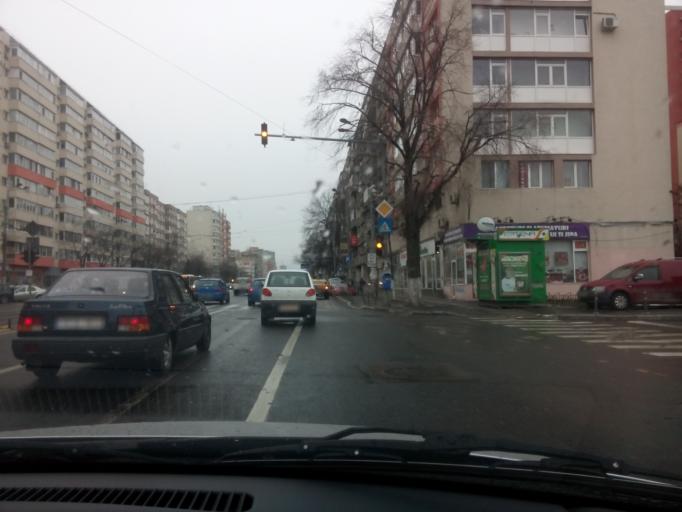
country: RO
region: Bucuresti
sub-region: Municipiul Bucuresti
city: Bucharest
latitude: 44.4530
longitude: 26.1096
